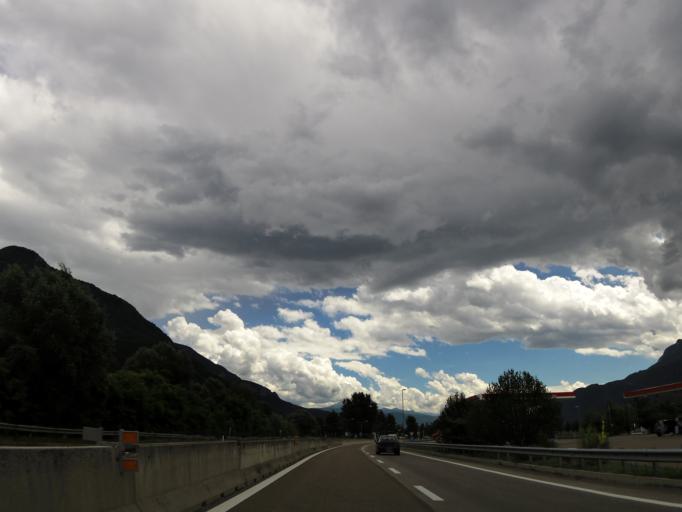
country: IT
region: Trentino-Alto Adige
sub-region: Bolzano
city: Nalles
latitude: 46.5647
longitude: 11.2139
